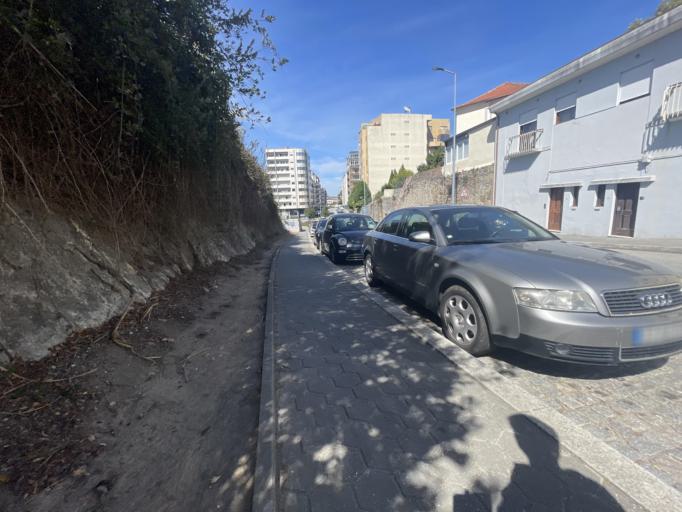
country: PT
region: Porto
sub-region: Vila Nova de Gaia
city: Vila Nova de Gaia
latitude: 41.1352
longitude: -8.6254
